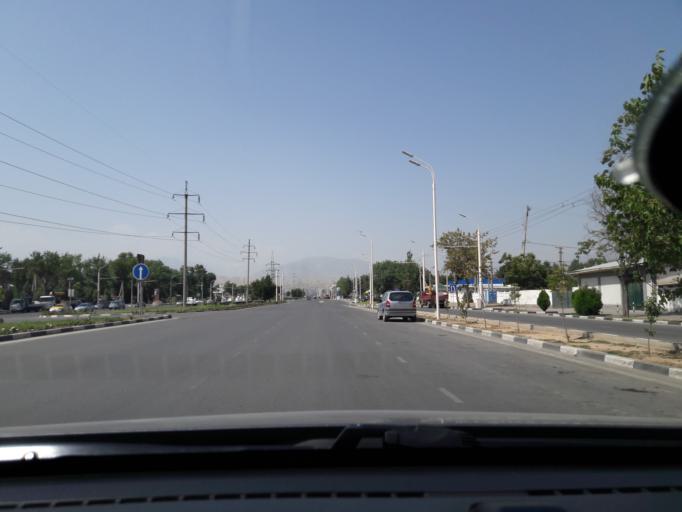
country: TJ
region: Dushanbe
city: Dushanbe
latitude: 38.5422
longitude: 68.7414
